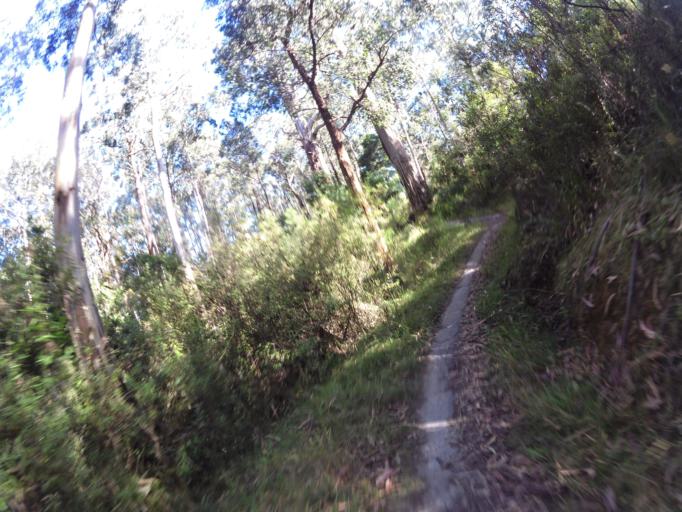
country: AU
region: Victoria
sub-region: Colac-Otway
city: Apollo Bay
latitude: -38.5351
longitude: 143.7286
